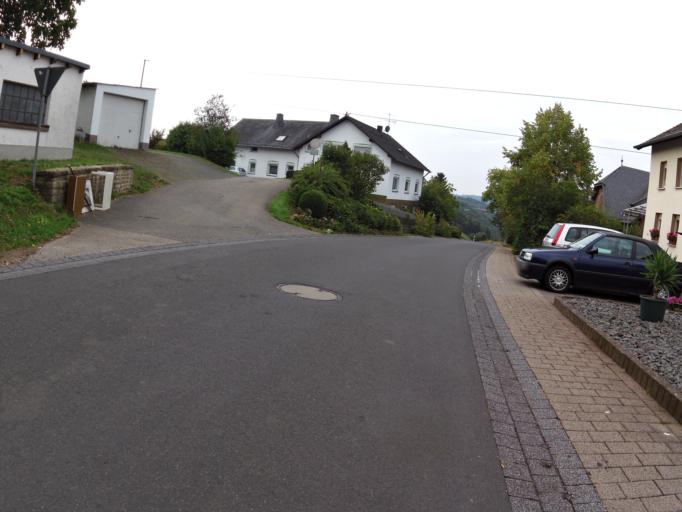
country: DE
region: Rheinland-Pfalz
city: Wilsecker
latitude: 50.0248
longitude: 6.5826
